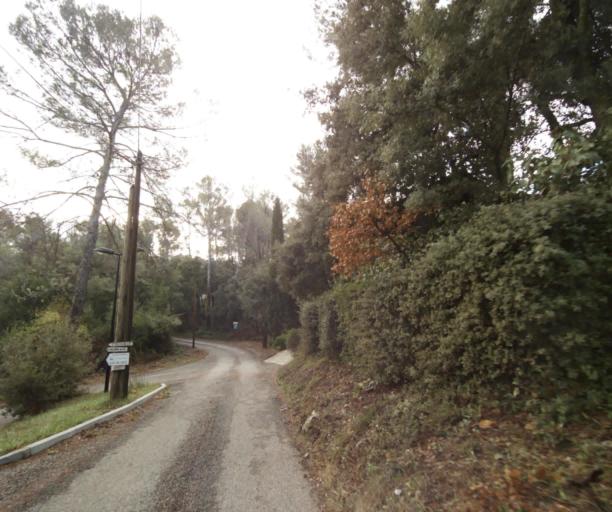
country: FR
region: Provence-Alpes-Cote d'Azur
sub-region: Departement du Var
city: Trans-en-Provence
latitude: 43.4899
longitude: 6.4990
